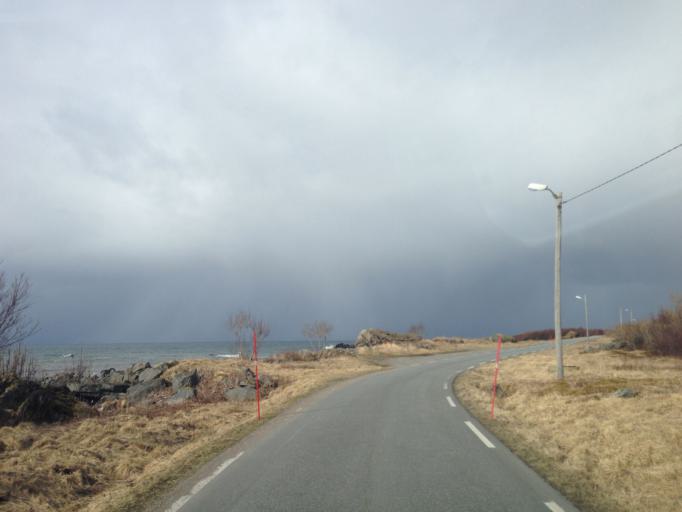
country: NO
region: Nordland
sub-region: Vagan
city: Svolvaer
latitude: 68.3990
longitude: 14.4976
